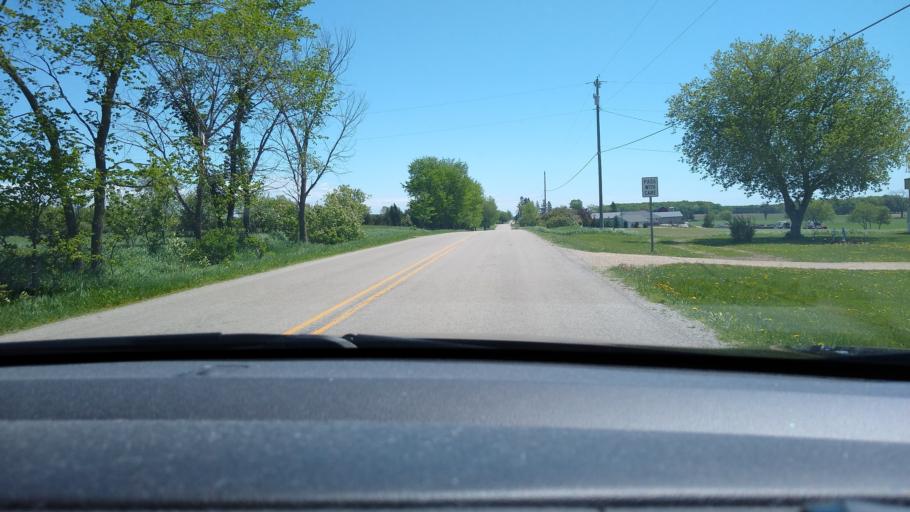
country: US
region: Michigan
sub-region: Delta County
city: Escanaba
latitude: 45.8261
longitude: -87.1502
